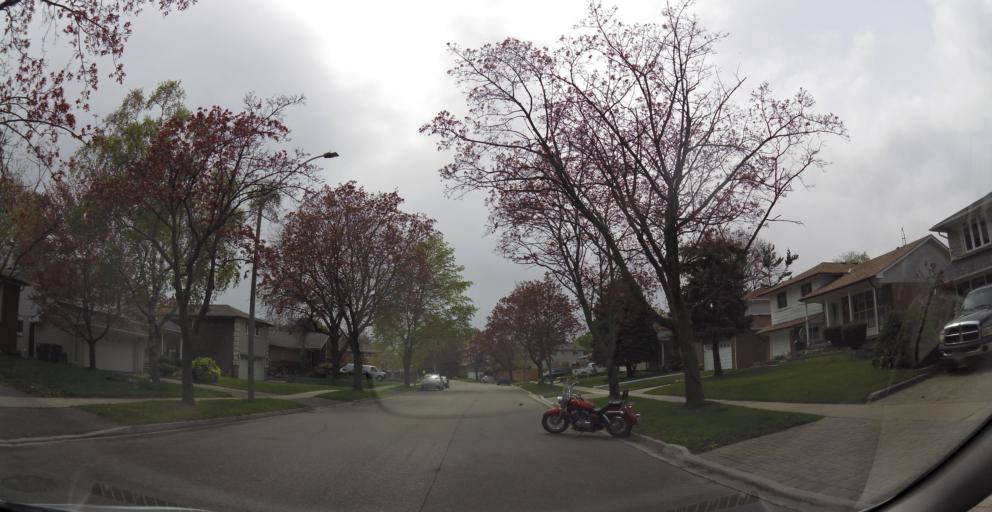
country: CA
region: Ontario
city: Mississauga
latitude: 43.5808
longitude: -79.5947
